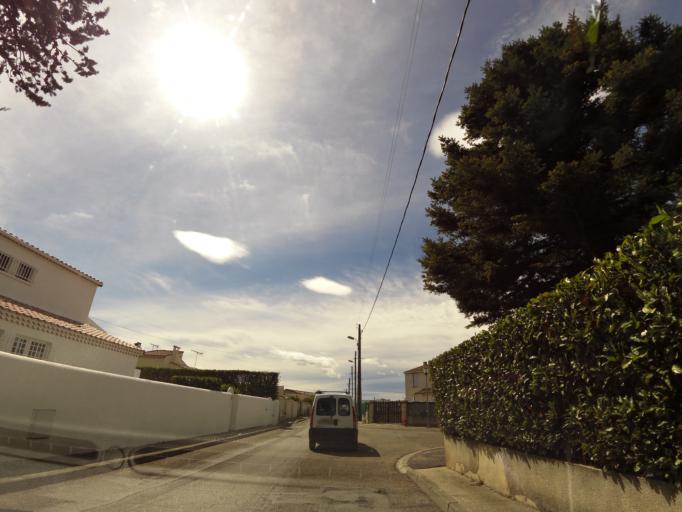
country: FR
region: Languedoc-Roussillon
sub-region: Departement du Gard
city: Milhaud
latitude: 43.7856
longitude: 4.3040
